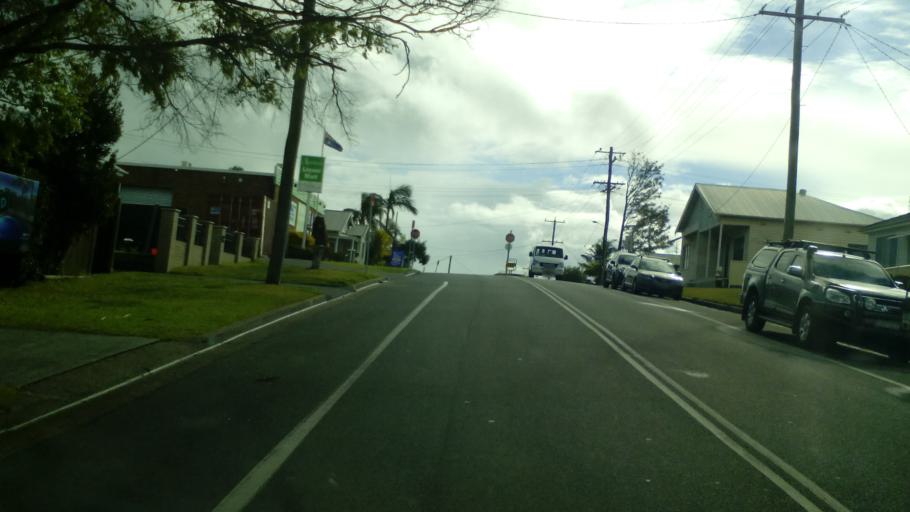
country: AU
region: New South Wales
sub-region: Lake Macquarie Shire
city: Kahibah
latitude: -32.9619
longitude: 151.7131
